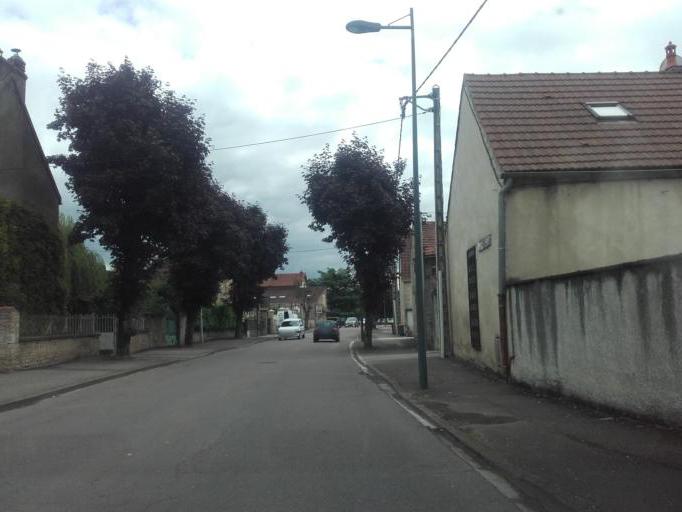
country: FR
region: Bourgogne
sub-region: Departement de la Cote-d'Or
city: Beaune
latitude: 47.0155
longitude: 4.8456
